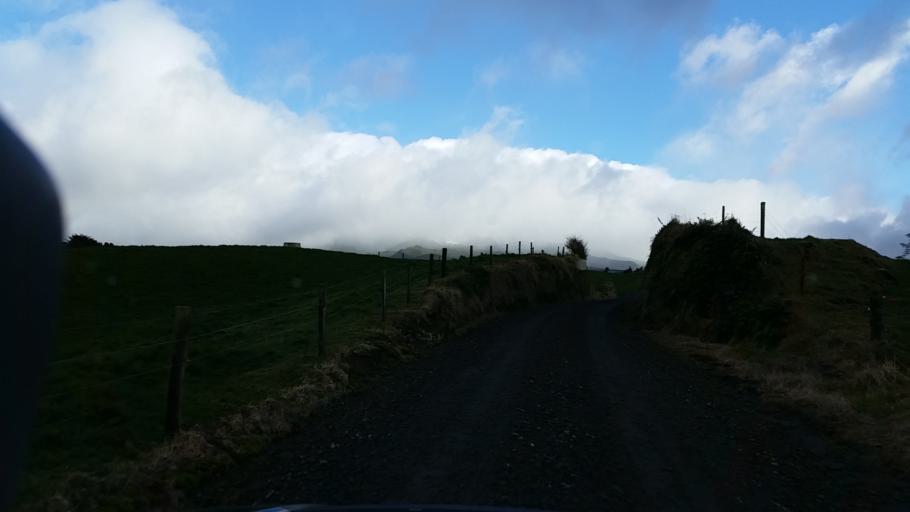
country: NZ
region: Taranaki
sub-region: South Taranaki District
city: Eltham
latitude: -39.3328
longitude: 174.1743
